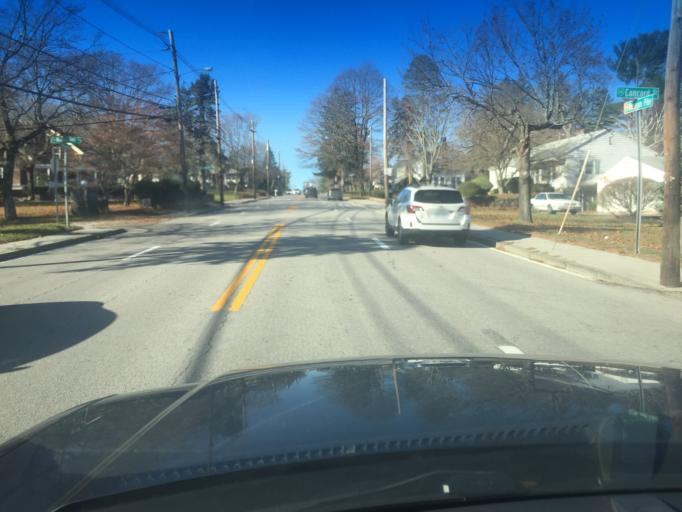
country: US
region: Rhode Island
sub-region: Providence County
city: Greenville
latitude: 41.8703
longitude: -71.5413
